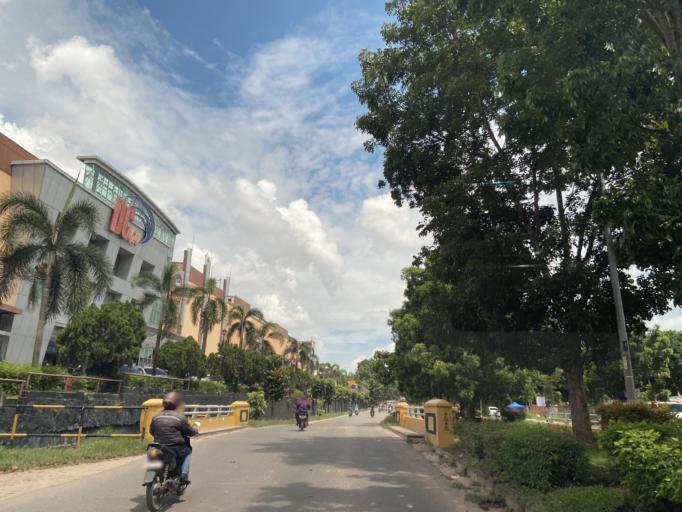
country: SG
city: Singapore
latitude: 1.1420
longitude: 104.0030
